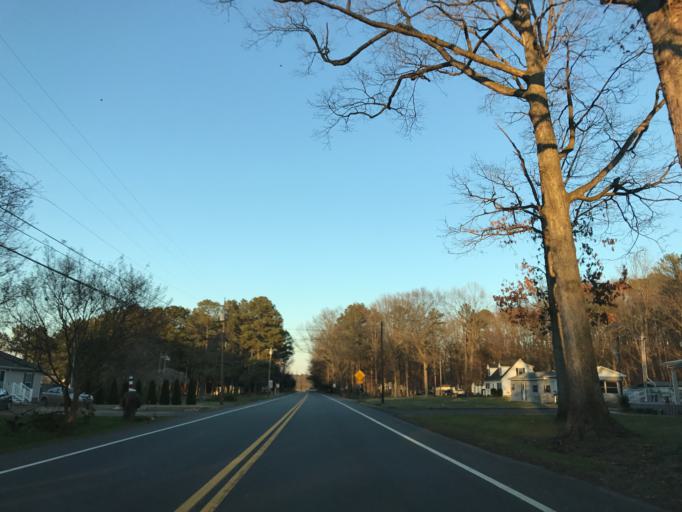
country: US
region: Maryland
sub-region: Talbot County
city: Easton
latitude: 38.8128
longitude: -76.0563
